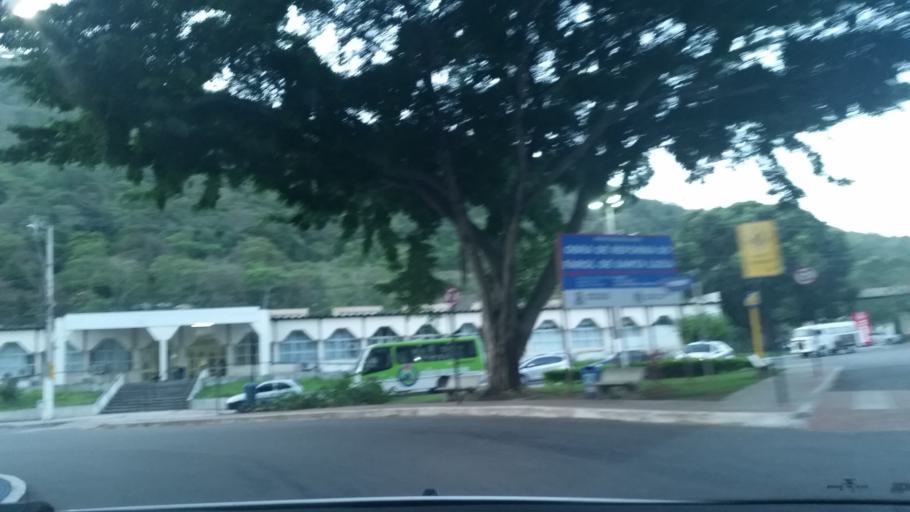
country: BR
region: Espirito Santo
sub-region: Vila Velha
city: Vila Velha
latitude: -20.3283
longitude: -40.2735
